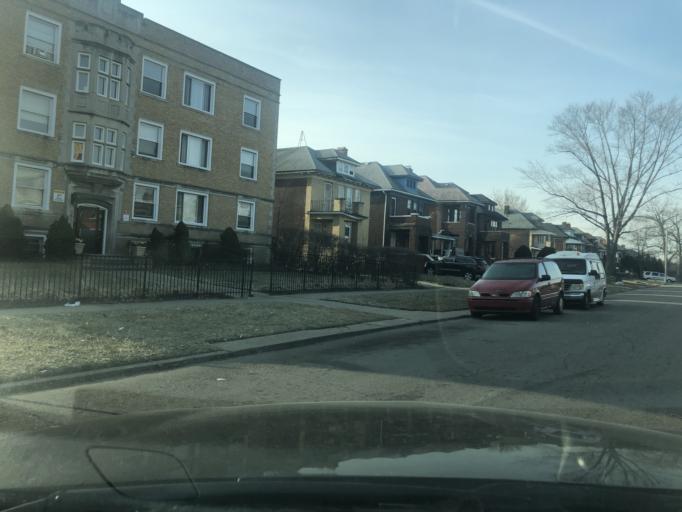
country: US
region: Michigan
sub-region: Wayne County
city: Highland Park
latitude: 42.3867
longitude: -83.1213
